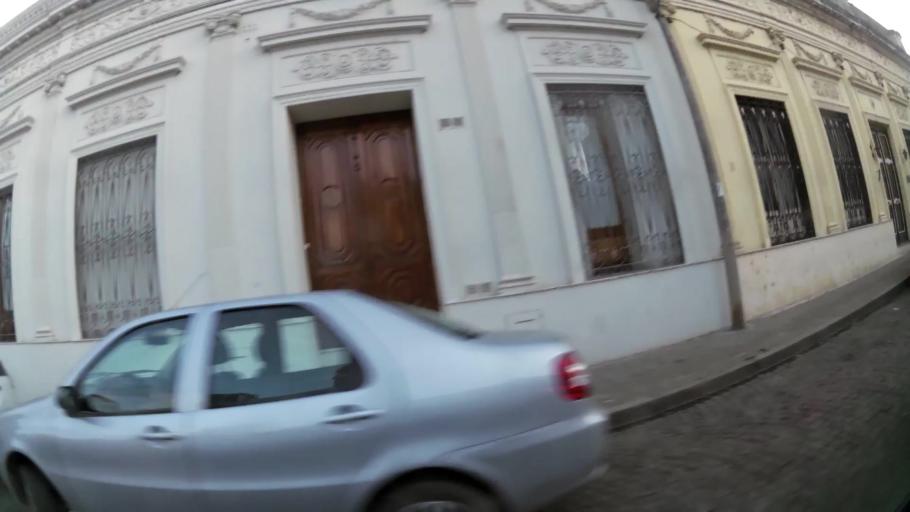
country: AR
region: Buenos Aires
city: San Nicolas de los Arroyos
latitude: -33.3270
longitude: -60.2193
